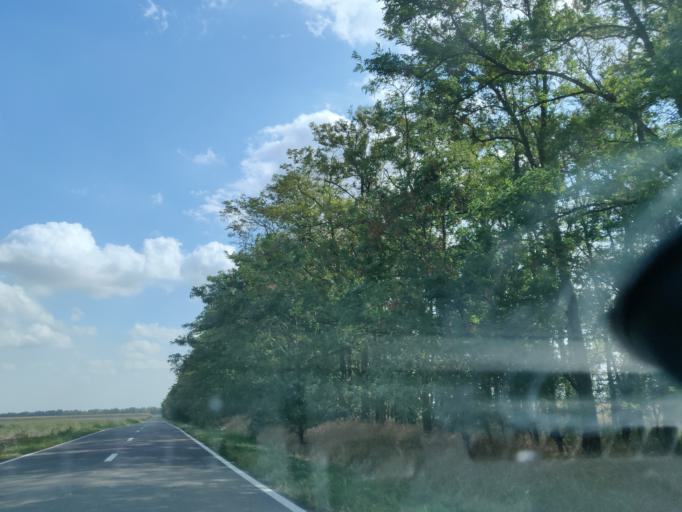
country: RO
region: Vrancea
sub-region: Comuna Ciorasti
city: Mihalceni
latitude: 45.4520
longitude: 27.3868
